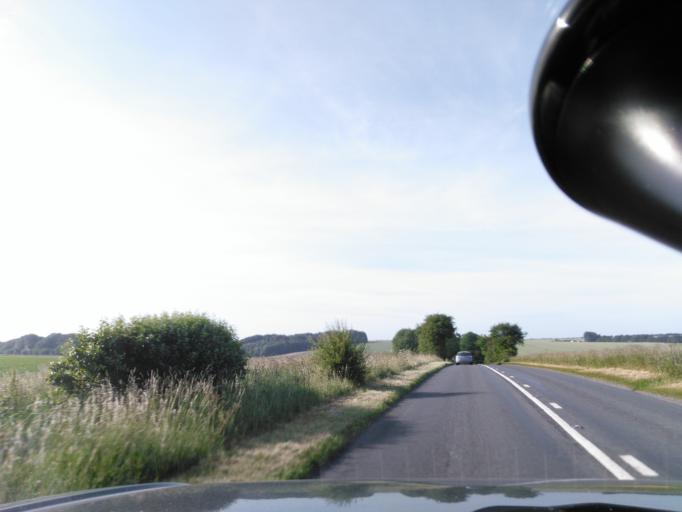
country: GB
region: England
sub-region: Wiltshire
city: Woodford
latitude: 51.1449
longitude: -1.8588
